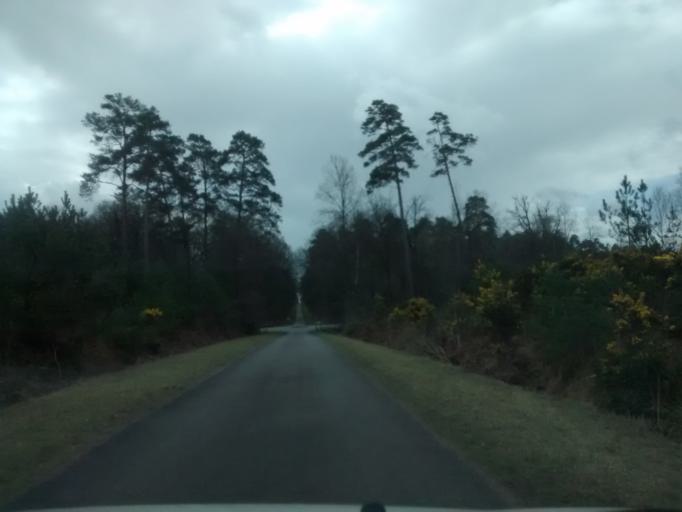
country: FR
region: Brittany
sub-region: Departement d'Ille-et-Vilaine
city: Fouillard
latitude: 48.1765
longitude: -1.5463
